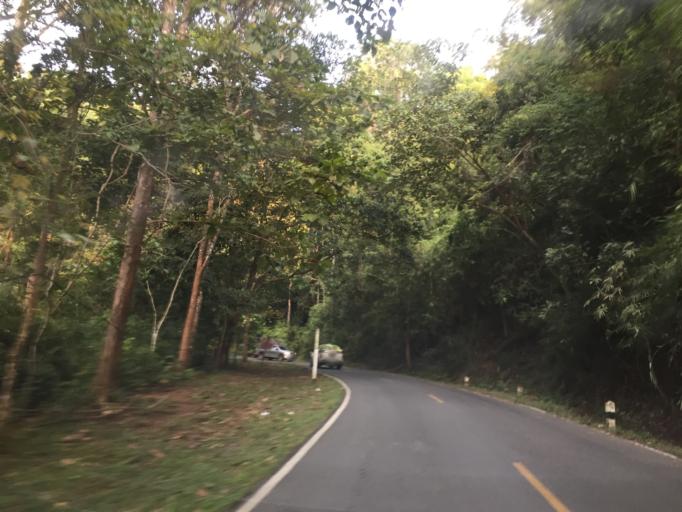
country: TH
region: Chiang Mai
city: Samoeng
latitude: 18.9587
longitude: 98.8365
